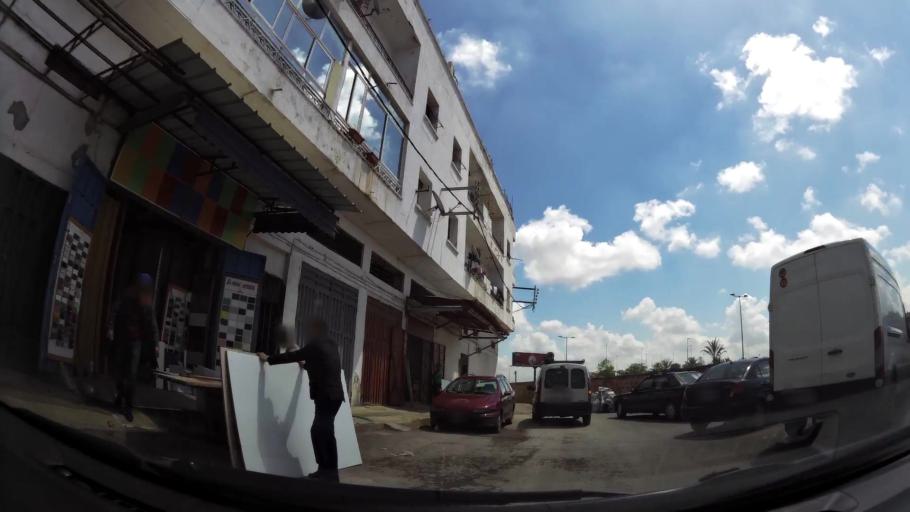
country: MA
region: Grand Casablanca
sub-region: Casablanca
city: Casablanca
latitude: 33.5594
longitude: -7.5966
